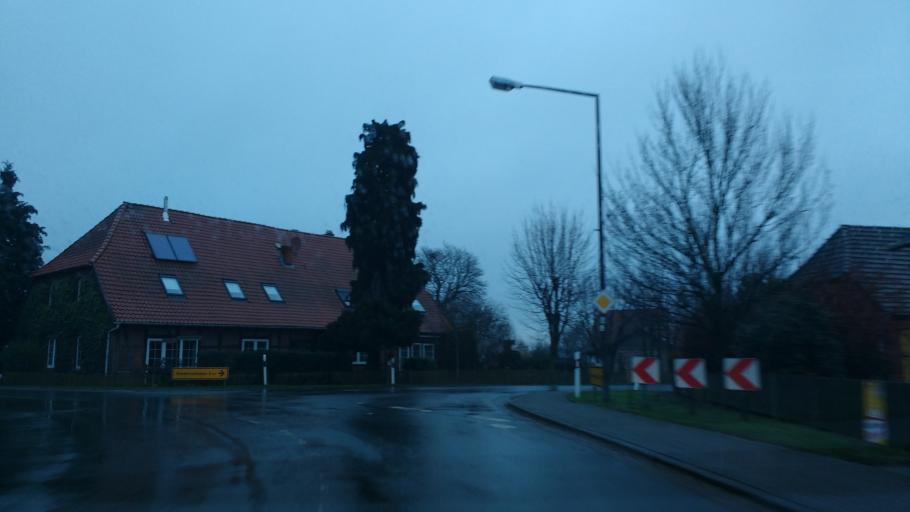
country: DE
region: Lower Saxony
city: Gilten
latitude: 52.6391
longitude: 9.5025
